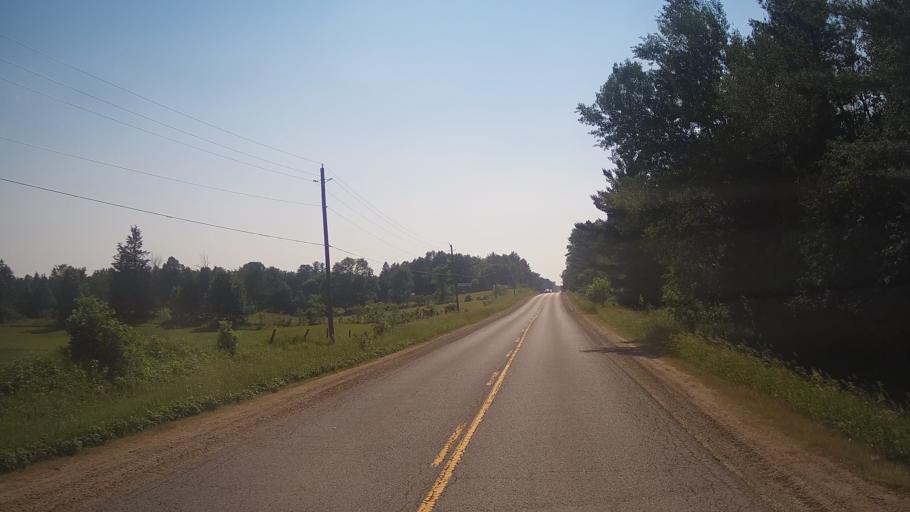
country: CA
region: Ontario
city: Pembroke
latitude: 45.6098
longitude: -77.2054
